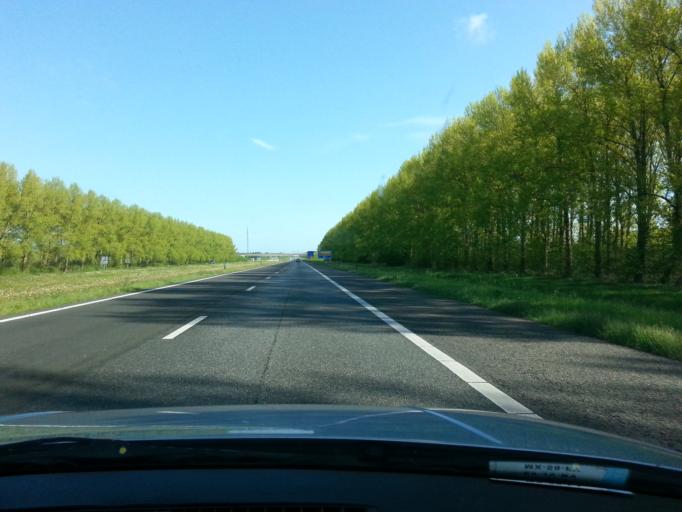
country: NL
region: Flevoland
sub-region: Gemeente Lelystad
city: Lelystad
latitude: 52.5348
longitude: 5.5328
